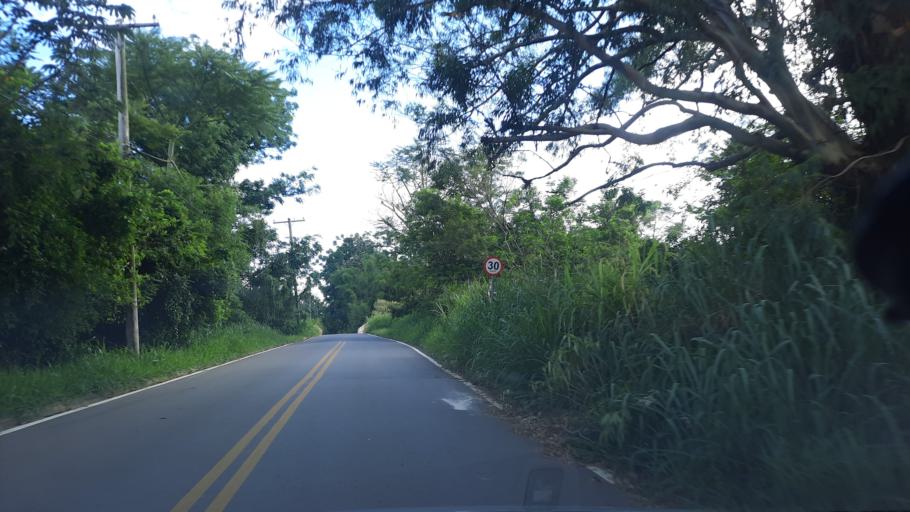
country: BR
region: Sao Paulo
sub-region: Atibaia
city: Atibaia
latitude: -23.1012
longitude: -46.5212
